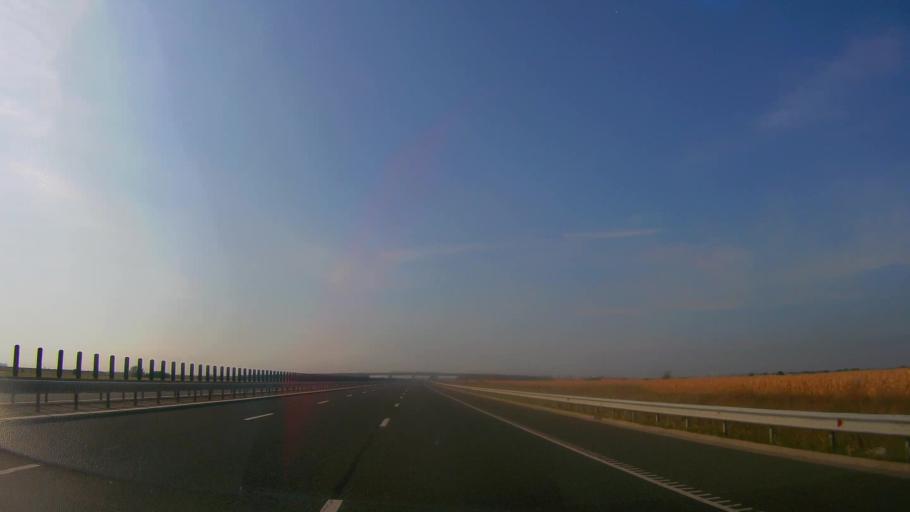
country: RO
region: Ilfov
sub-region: Comuna Tunari
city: Tunari
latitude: 44.5680
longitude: 26.1808
